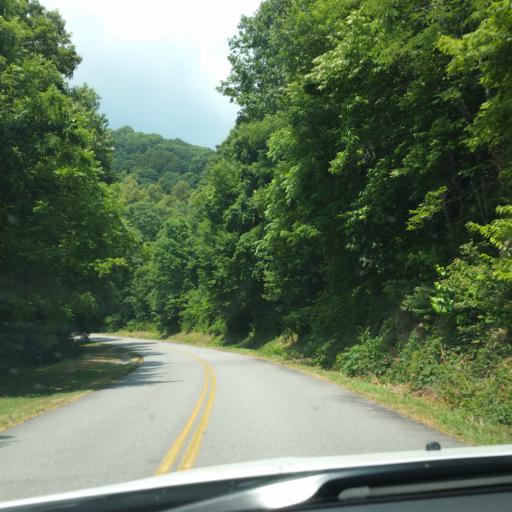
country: US
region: North Carolina
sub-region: Buncombe County
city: Bent Creek
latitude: 35.4736
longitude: -82.6204
